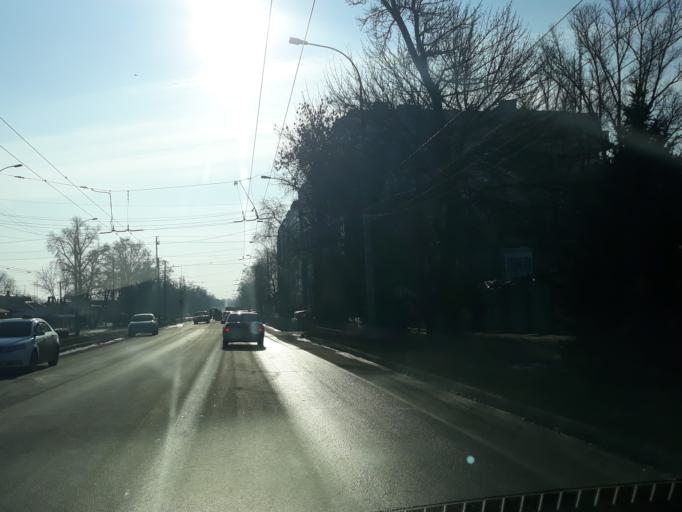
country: RU
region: Rostov
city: Taganrog
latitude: 47.2296
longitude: 38.9071
